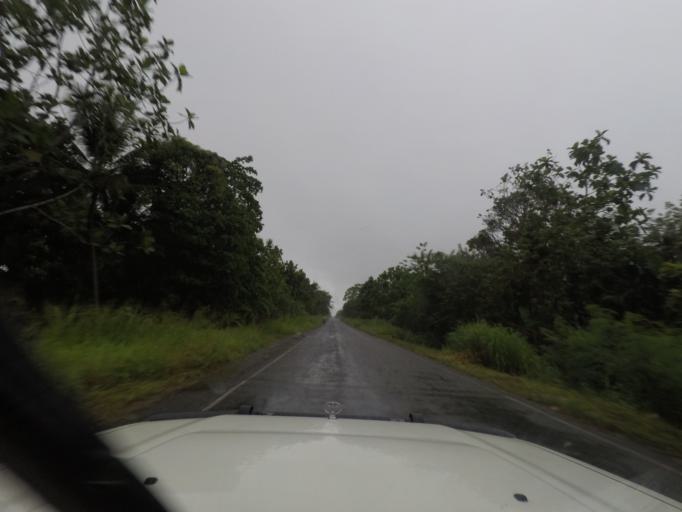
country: PG
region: Madang
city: Madang
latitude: -5.3847
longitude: 145.6914
